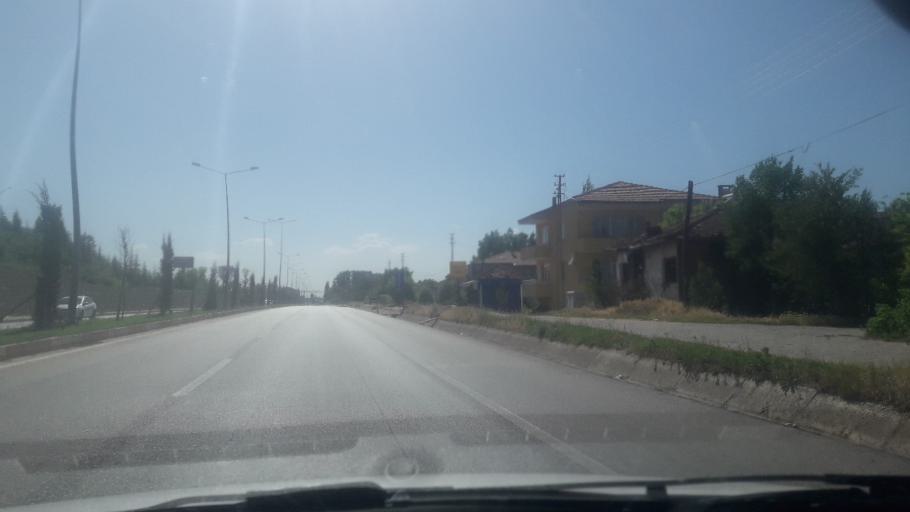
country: TR
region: Tokat
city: Tokat
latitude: 40.3354
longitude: 36.4818
